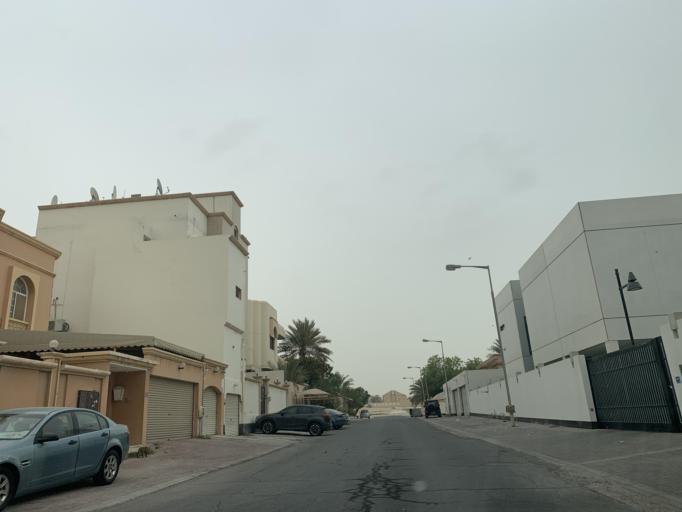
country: BH
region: Central Governorate
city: Madinat Hamad
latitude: 26.1470
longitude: 50.5234
